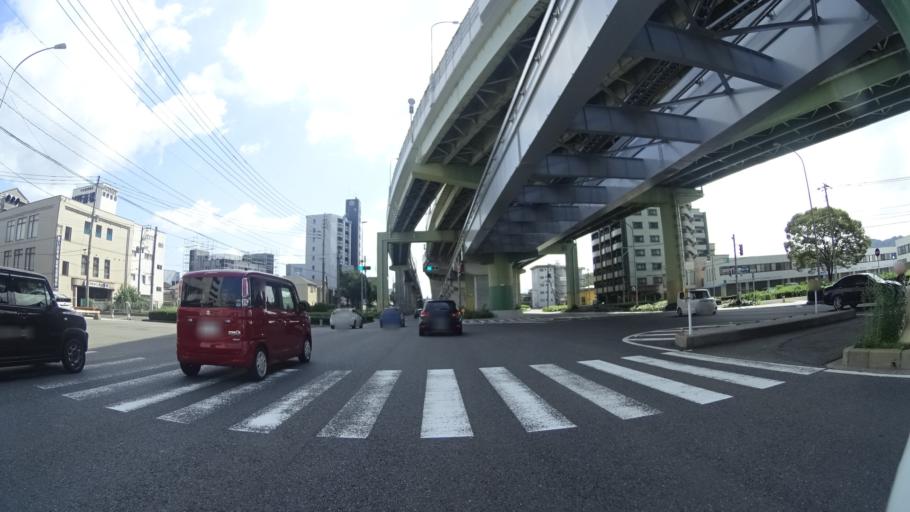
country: JP
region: Fukuoka
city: Kitakyushu
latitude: 33.8560
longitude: 130.8793
